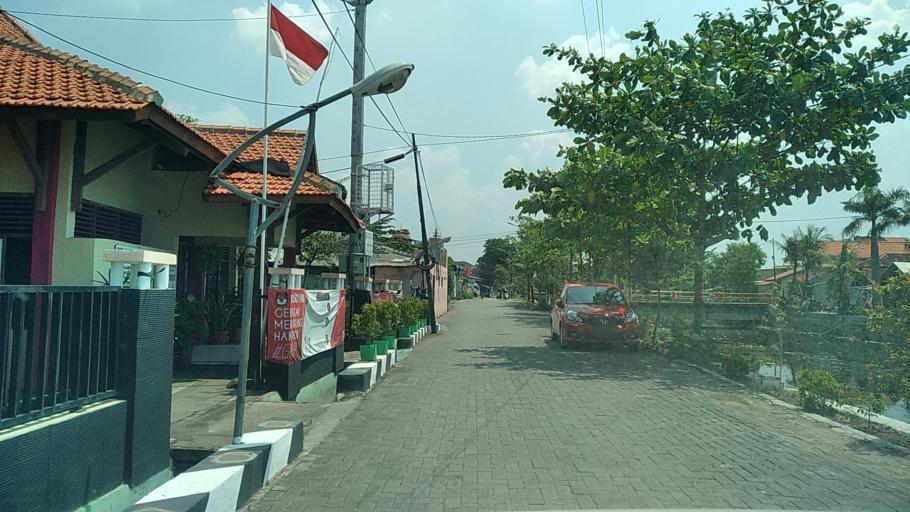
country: ID
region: Central Java
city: Semarang
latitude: -6.9653
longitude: 110.4405
